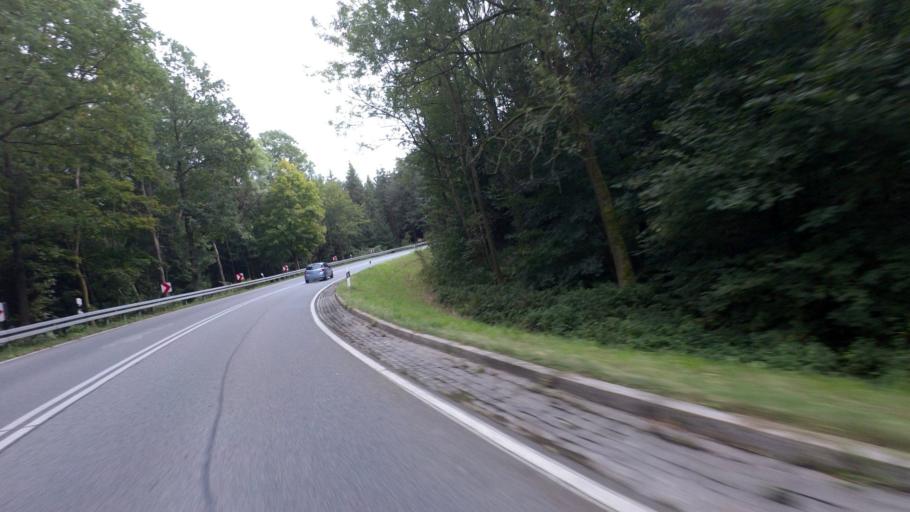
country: DE
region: Saxony
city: Oppach
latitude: 51.0791
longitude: 14.4891
